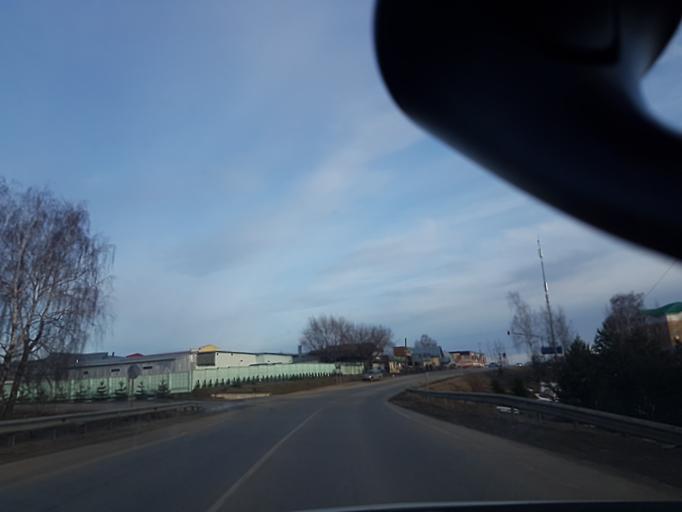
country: RU
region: Moskovskaya
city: Istra
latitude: 55.8996
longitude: 36.8596
